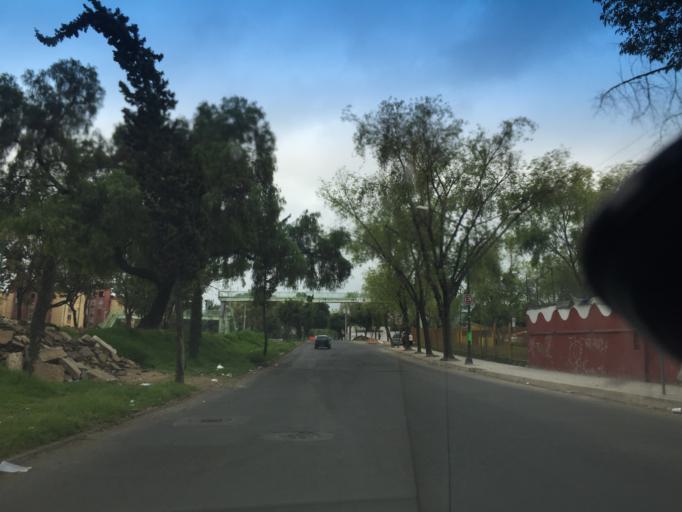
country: MX
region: Mexico City
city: Azcapotzalco
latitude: 19.5099
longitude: -99.1918
